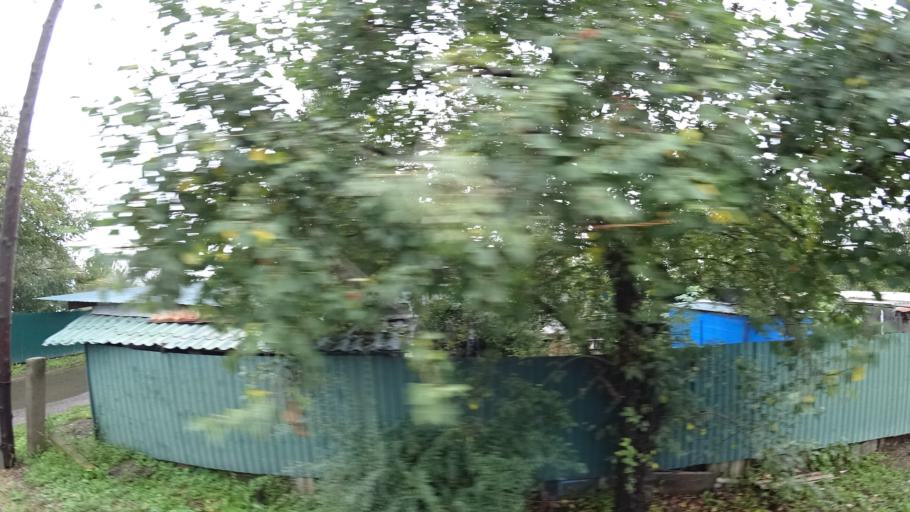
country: RU
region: Primorskiy
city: Monastyrishche
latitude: 44.1919
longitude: 132.4201
